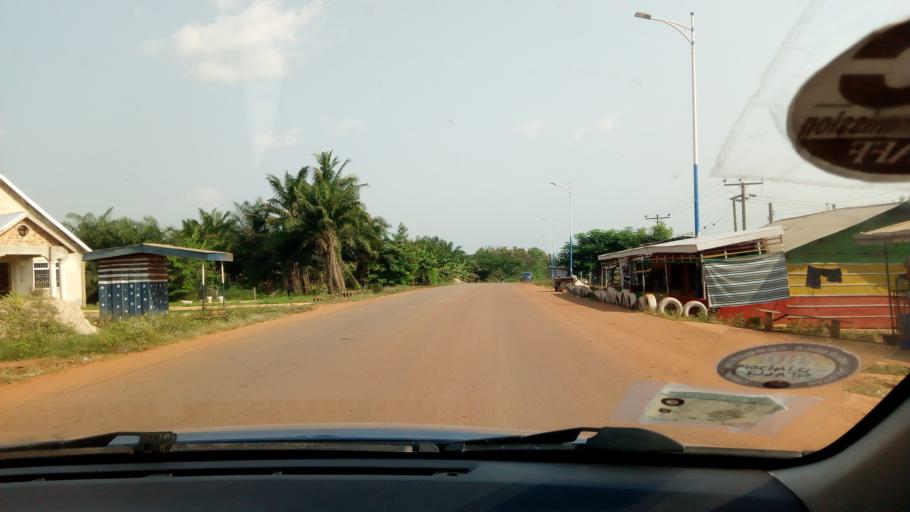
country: GH
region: Western
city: Bibiani
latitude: 6.8051
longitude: -2.5252
